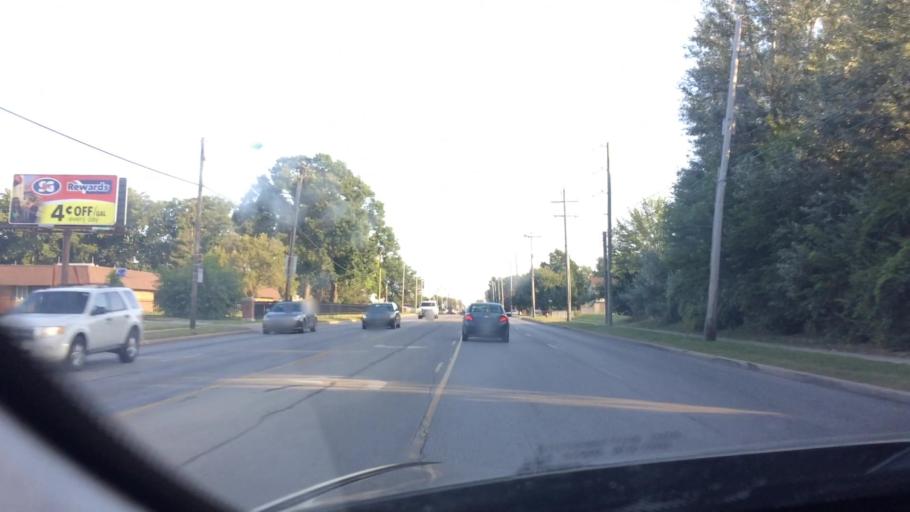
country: US
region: Ohio
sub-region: Lucas County
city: Ottawa Hills
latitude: 41.6454
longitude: -83.6260
